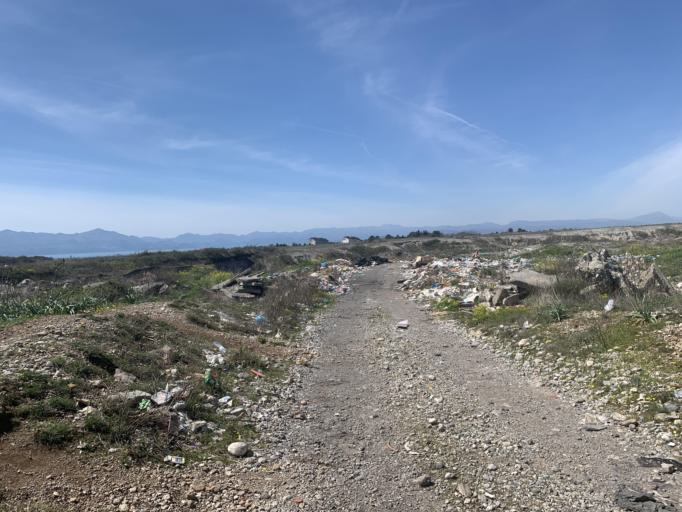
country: AL
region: Shkoder
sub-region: Rrethi i Malesia e Madhe
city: Koplik
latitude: 42.2296
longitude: 19.4343
